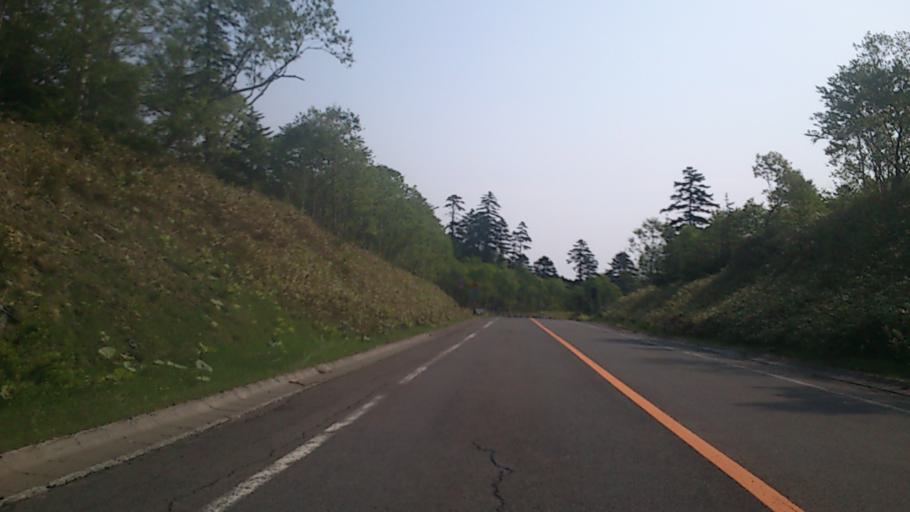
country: JP
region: Hokkaido
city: Bihoro
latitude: 43.4616
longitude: 144.2301
